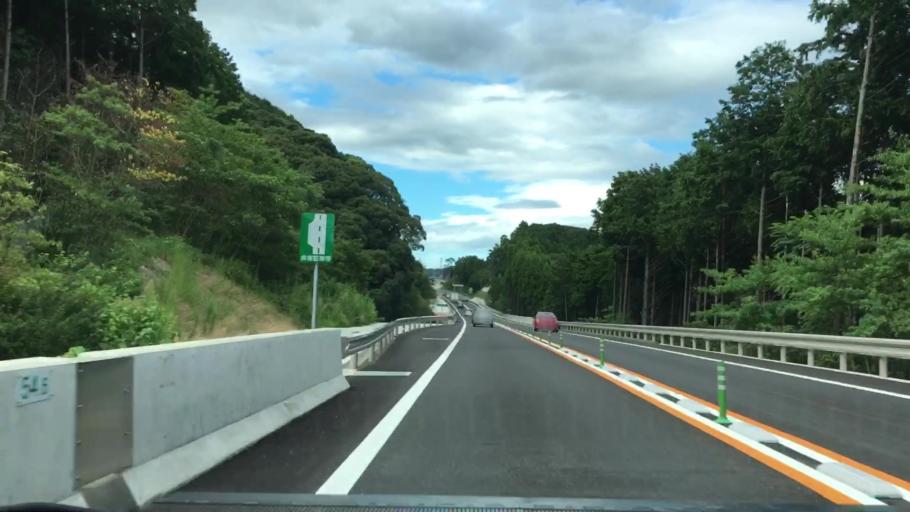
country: JP
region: Saga Prefecture
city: Imaricho-ko
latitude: 33.3261
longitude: 129.9273
